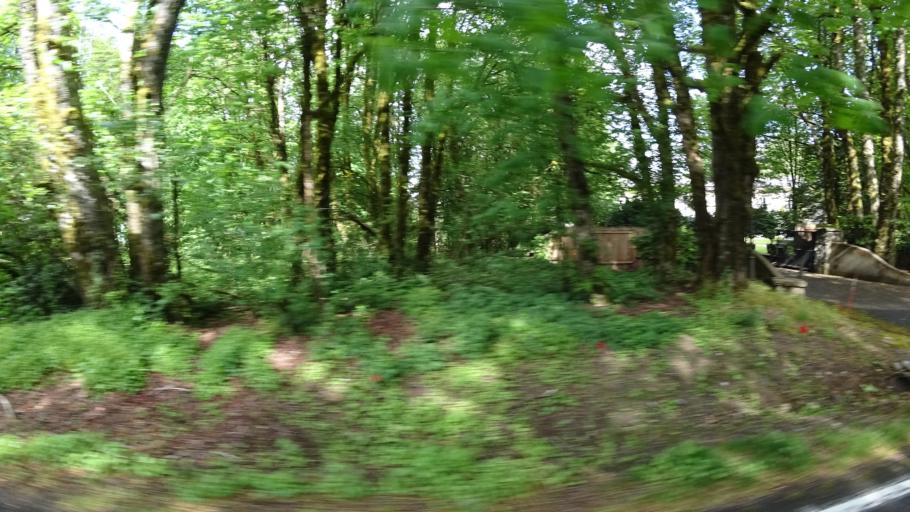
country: US
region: Oregon
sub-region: Washington County
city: West Haven
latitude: 45.5411
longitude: -122.7591
